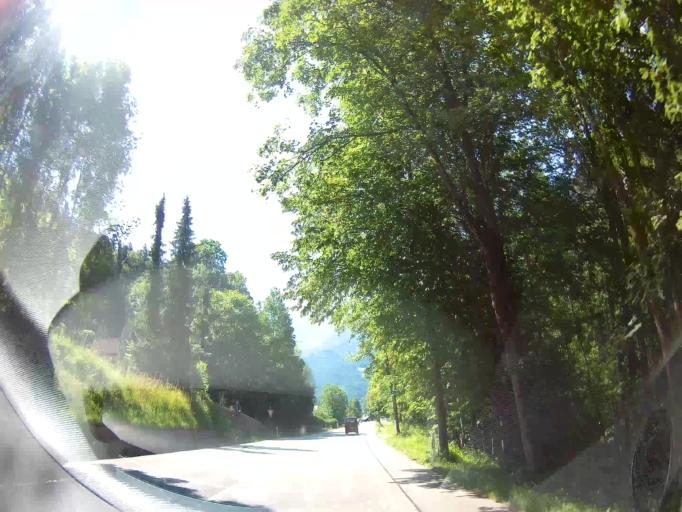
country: DE
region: Bavaria
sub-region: Upper Bavaria
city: Marktschellenberg
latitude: 47.6622
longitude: 13.0367
